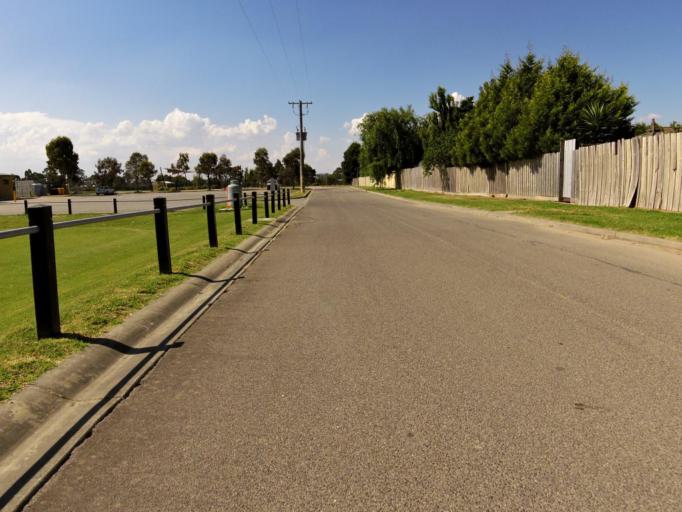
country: AU
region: Victoria
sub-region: Casey
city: Hampton Park
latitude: -38.0233
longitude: 145.2509
